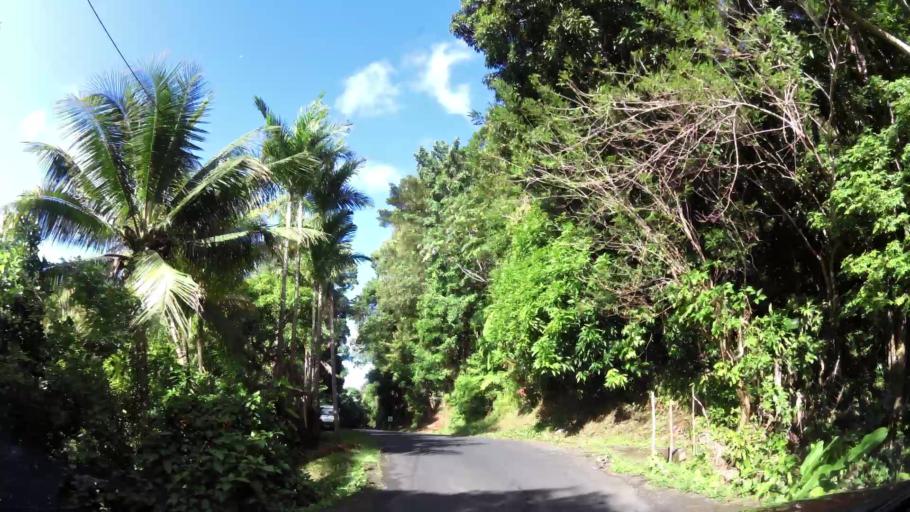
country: DM
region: Saint John
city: Portsmouth
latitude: 15.5746
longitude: -61.4334
